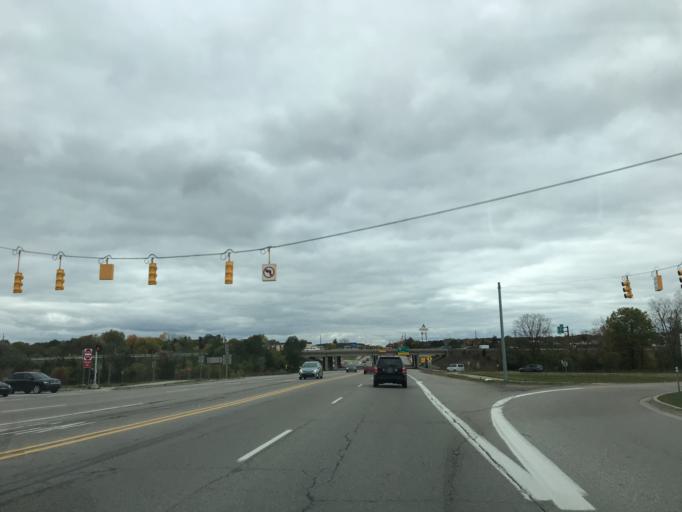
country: US
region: Michigan
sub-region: Washtenaw County
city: Ann Arbor
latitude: 42.2543
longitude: -83.6811
